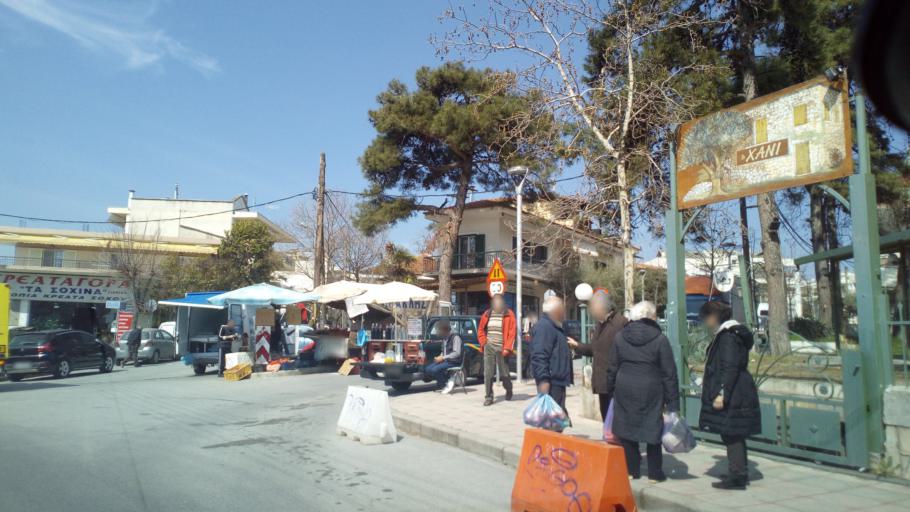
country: GR
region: Central Macedonia
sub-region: Nomos Thessalonikis
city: Thermi
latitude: 40.5504
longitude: 23.0214
